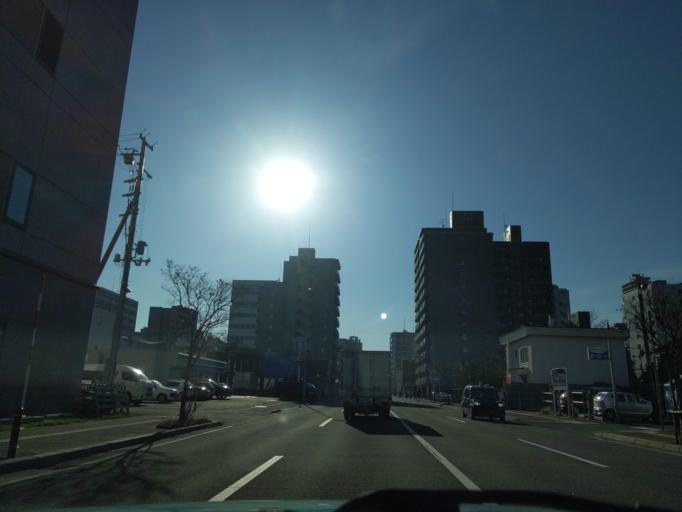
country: JP
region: Hokkaido
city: Sapporo
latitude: 43.0664
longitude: 141.3329
